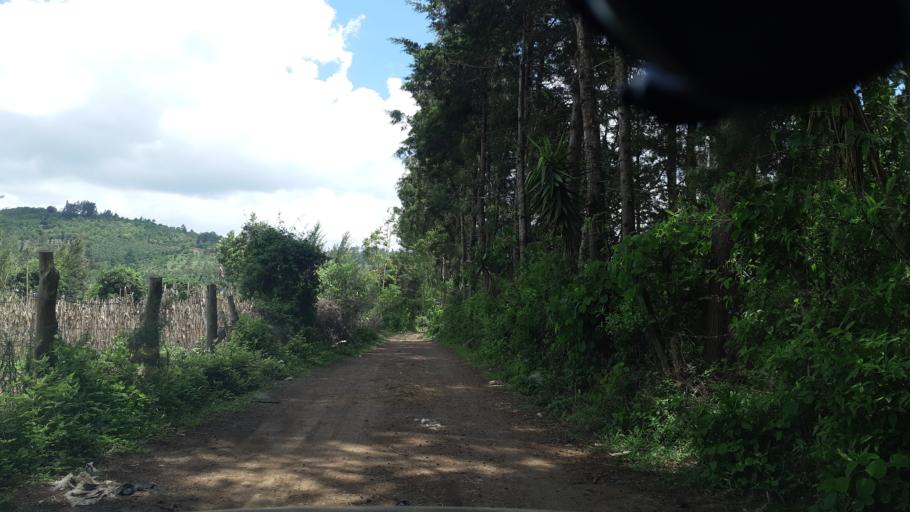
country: GT
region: Chimaltenango
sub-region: Municipio de Chimaltenango
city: Chimaltenango
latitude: 14.6574
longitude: -90.8482
